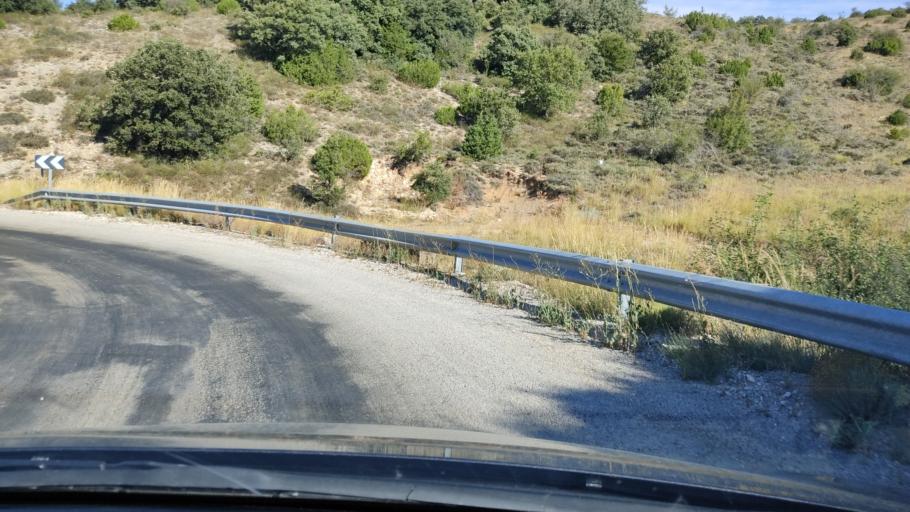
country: ES
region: Aragon
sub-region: Provincia de Teruel
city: Fonfria
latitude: 41.0036
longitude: -1.0700
